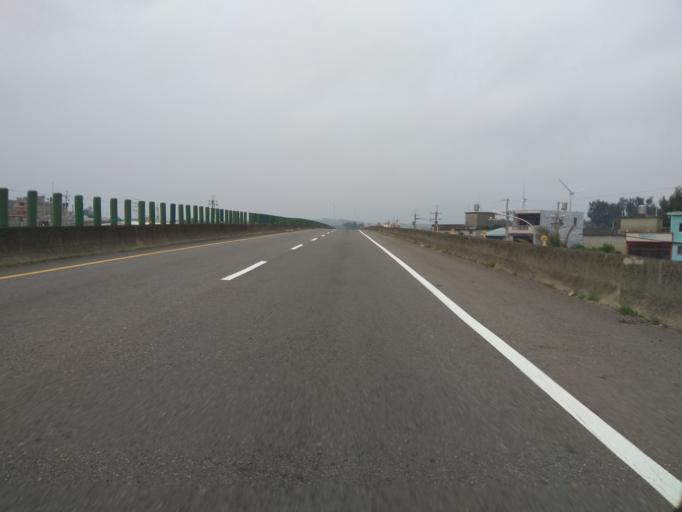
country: TW
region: Taiwan
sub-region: Miaoli
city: Miaoli
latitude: 24.6643
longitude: 120.8243
